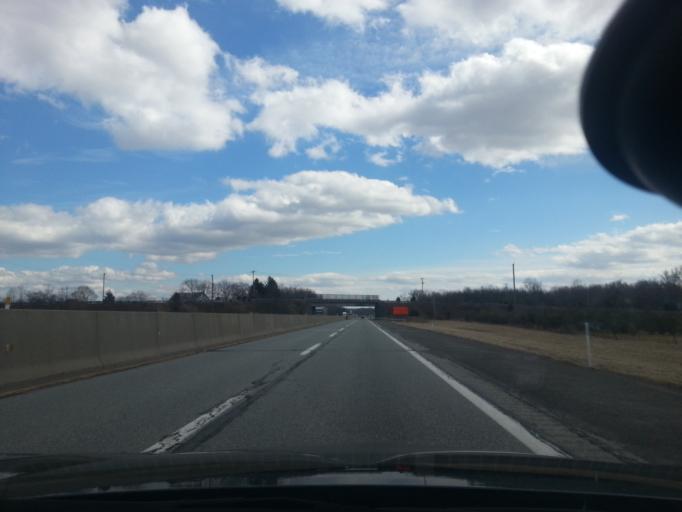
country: US
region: Pennsylvania
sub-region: Bucks County
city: Spinnerstown
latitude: 40.4456
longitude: -75.4324
